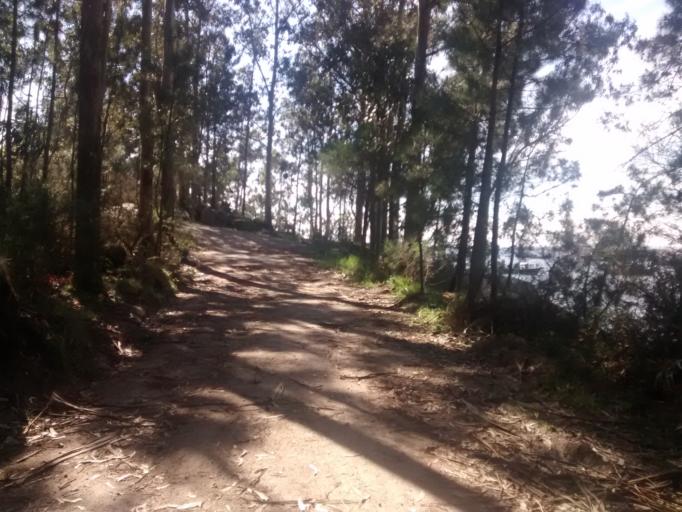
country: ES
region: Galicia
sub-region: Provincia de Pontevedra
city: O Grove
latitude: 42.4871
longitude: -8.8848
